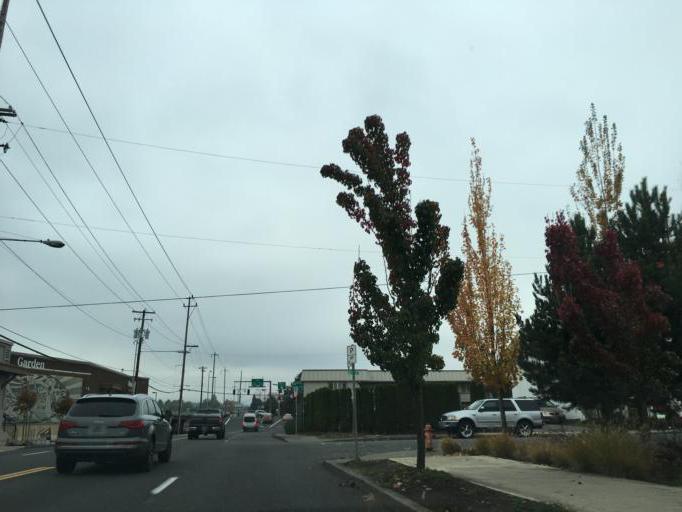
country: US
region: Oregon
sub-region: Multnomah County
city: Portland
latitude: 45.5338
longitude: -122.6210
